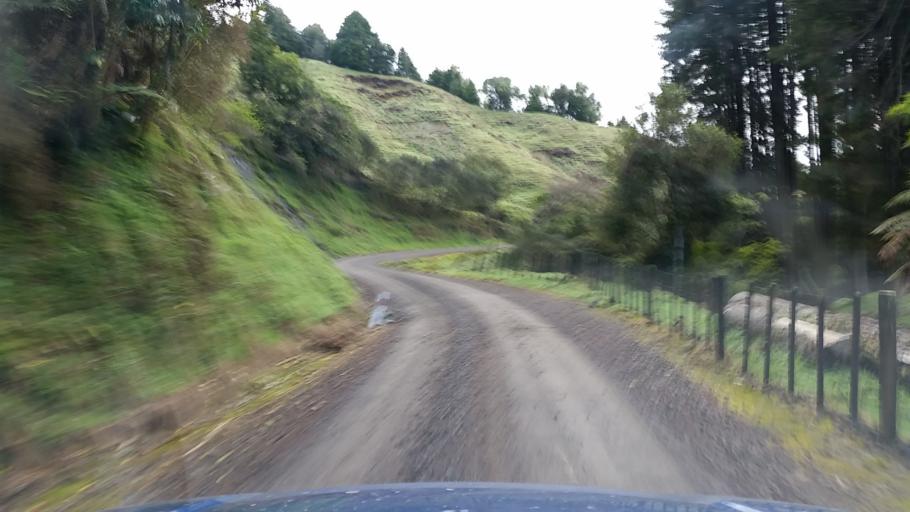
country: NZ
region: Taranaki
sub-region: New Plymouth District
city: Waitara
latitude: -39.0961
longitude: 174.8385
